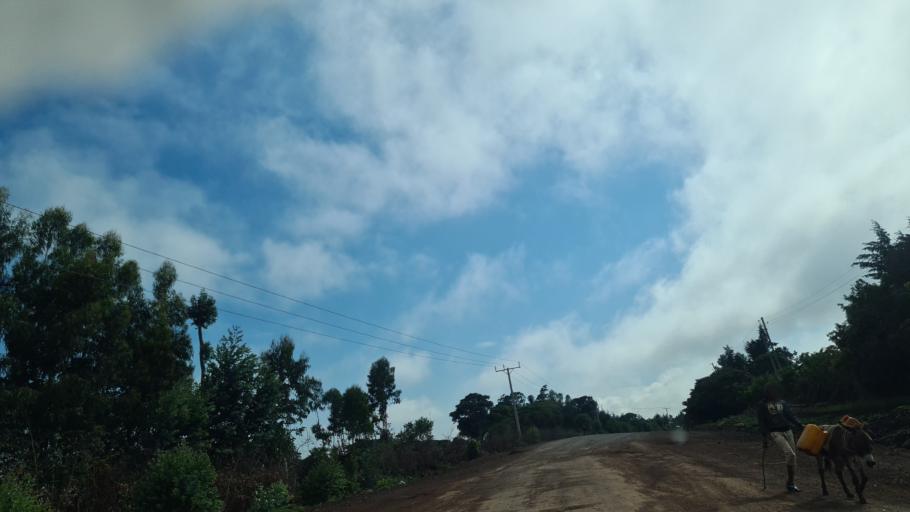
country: ET
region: Oromiya
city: Huruta
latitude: 8.1291
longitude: 39.3803
